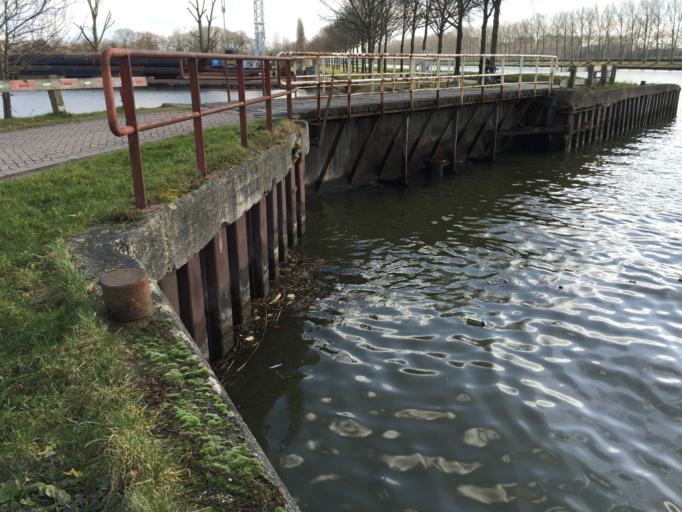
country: NL
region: Utrecht
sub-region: Stichtse Vecht
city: Spechtenkamp
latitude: 52.1429
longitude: 5.0244
